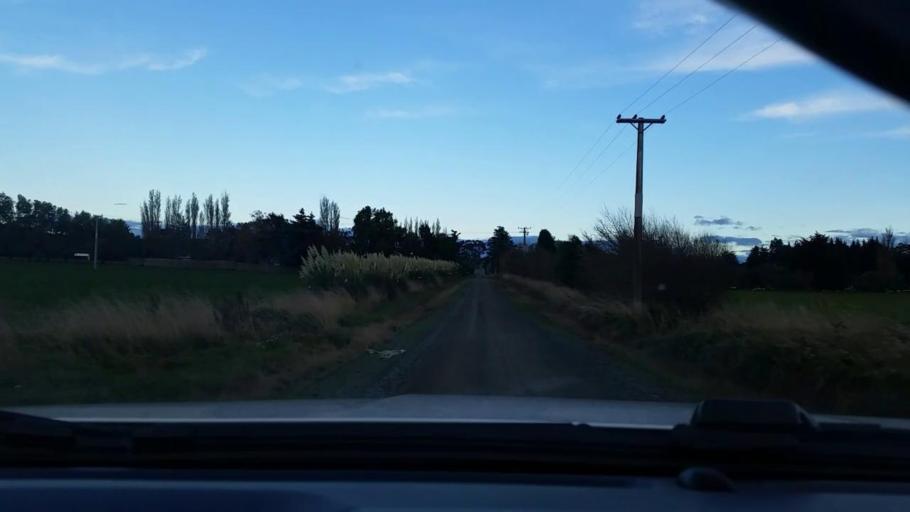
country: NZ
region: Southland
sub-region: Southland District
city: Winton
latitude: -46.1029
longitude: 168.4639
